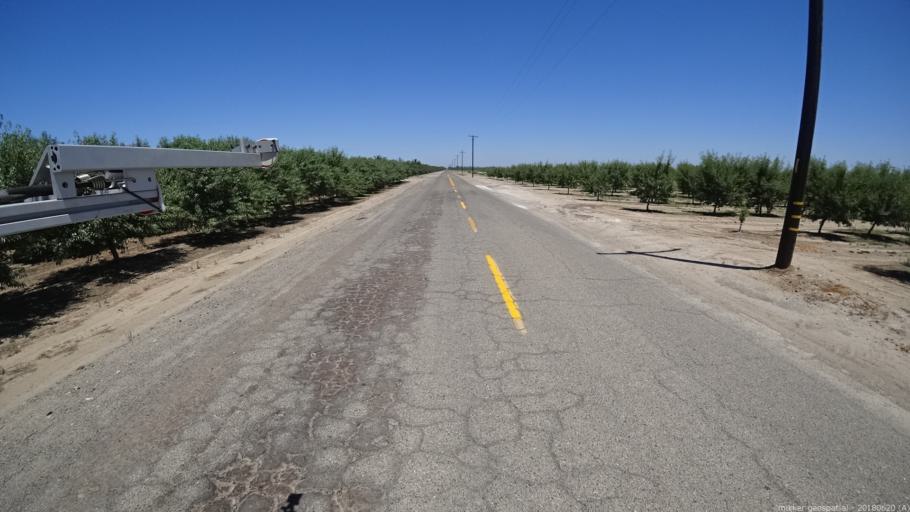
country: US
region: California
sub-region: Madera County
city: Parkwood
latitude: 36.8723
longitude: -120.0375
